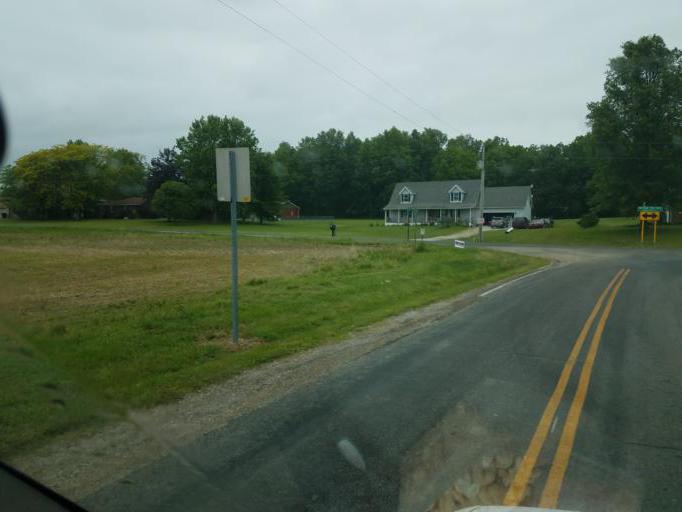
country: US
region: Ohio
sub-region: Marion County
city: Marion
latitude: 40.5530
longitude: -83.0177
